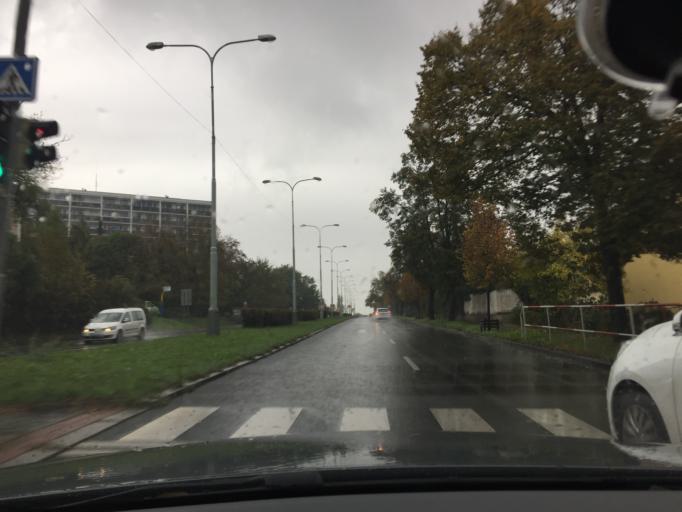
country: CZ
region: Praha
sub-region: Praha 8
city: Liben
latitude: 50.1296
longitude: 14.4521
